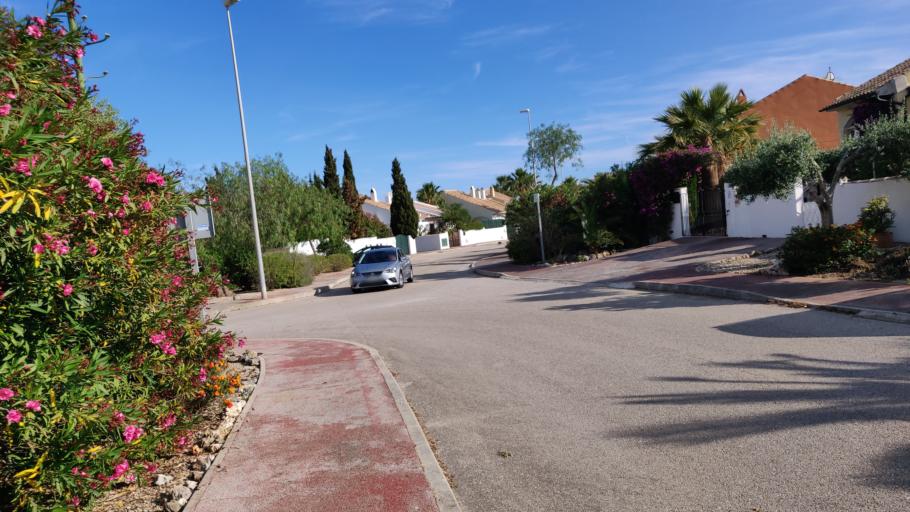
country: ES
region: Balearic Islands
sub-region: Illes Balears
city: Felanitx
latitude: 39.4523
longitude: 3.2603
